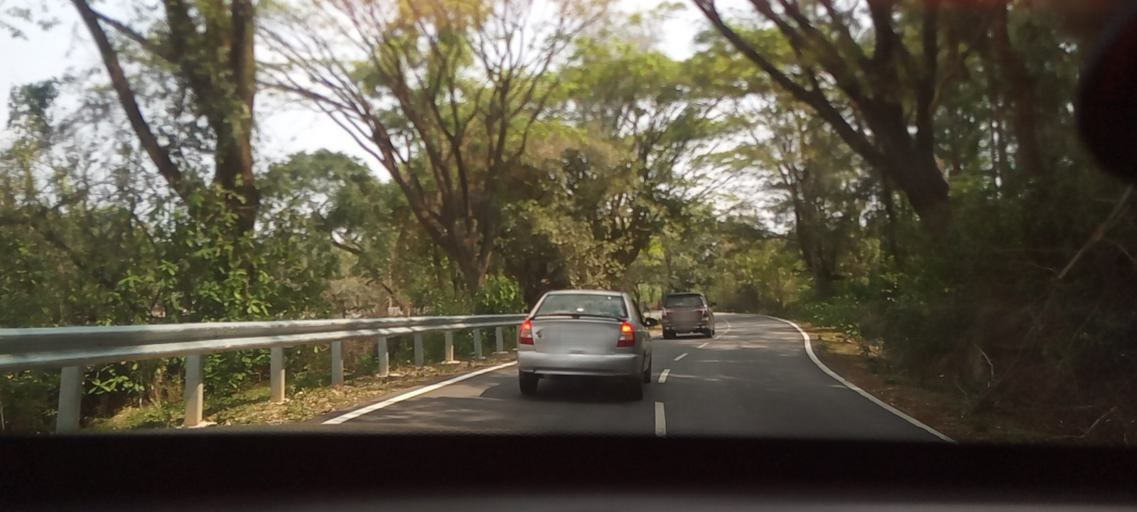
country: IN
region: Karnataka
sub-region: Chikmagalur
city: Chikmagalur
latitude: 13.2659
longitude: 75.7030
